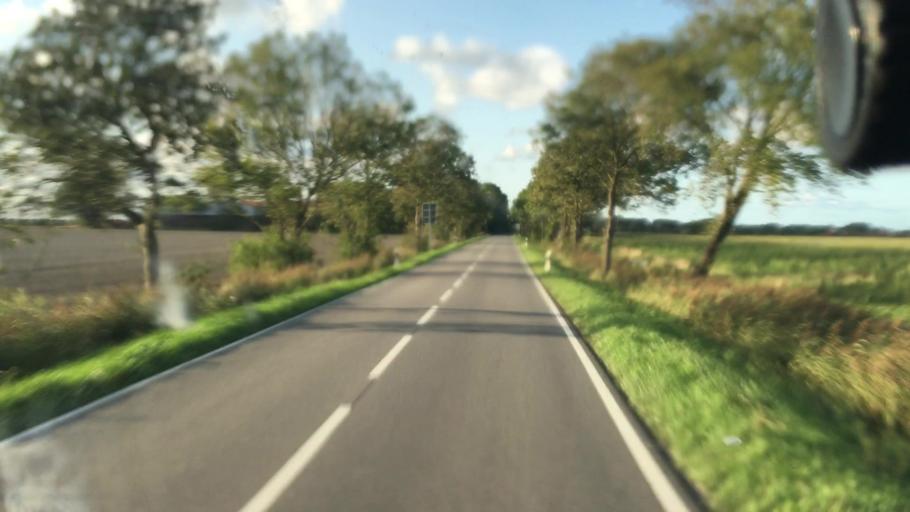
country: DE
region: Lower Saxony
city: Neuharlingersiel
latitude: 53.6856
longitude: 7.6871
